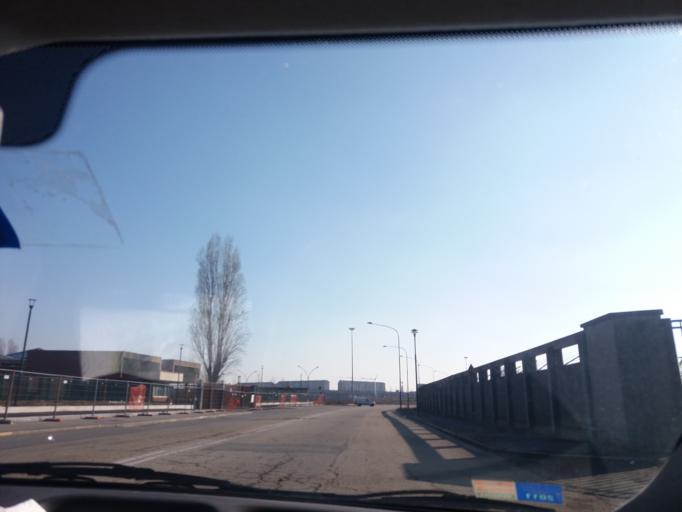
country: IT
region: Piedmont
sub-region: Provincia di Torino
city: Fornaci
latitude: 45.0292
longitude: 7.6086
